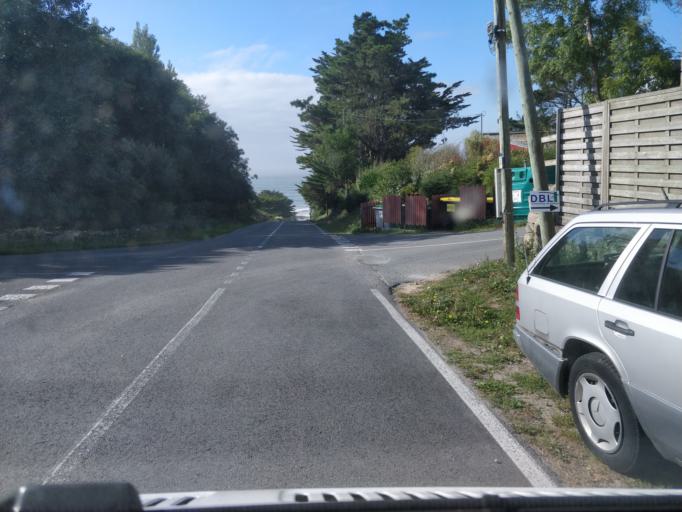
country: FR
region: Brittany
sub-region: Departement du Finistere
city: Plouhinec
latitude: 48.0054
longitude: -4.4963
